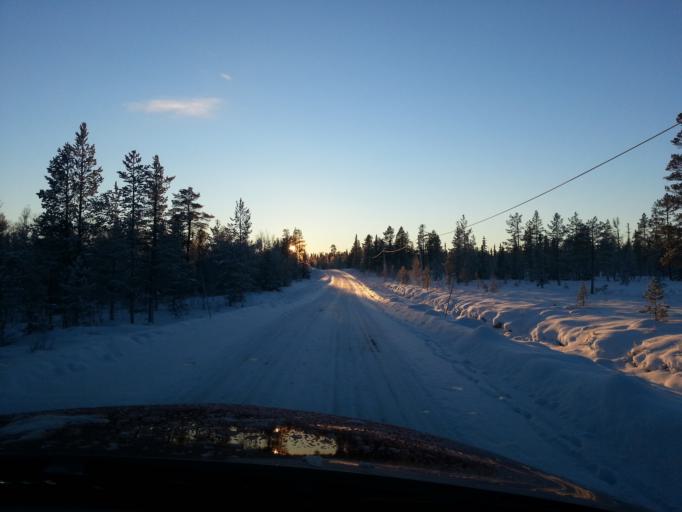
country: SE
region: Jaemtland
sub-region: Harjedalens Kommun
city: Sveg
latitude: 62.2830
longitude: 13.3966
